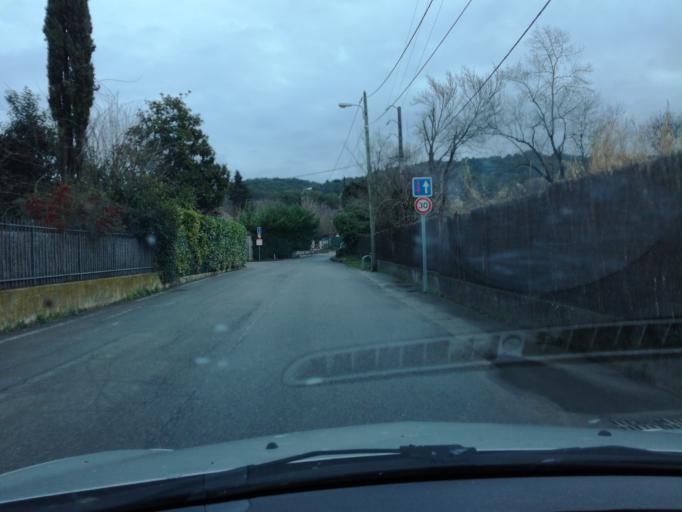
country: FR
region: Provence-Alpes-Cote d'Azur
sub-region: Departement des Alpes-Maritimes
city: Mouans-Sartoux
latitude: 43.6060
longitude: 6.9737
